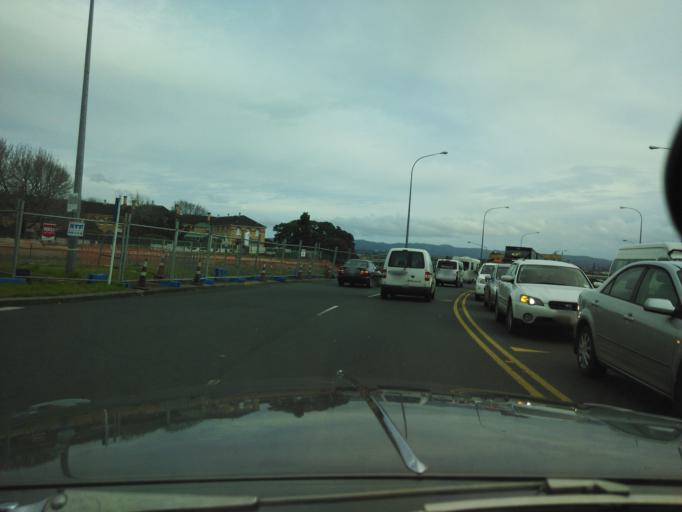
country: NZ
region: Auckland
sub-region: Auckland
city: Rosebank
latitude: -36.8710
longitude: 174.7097
